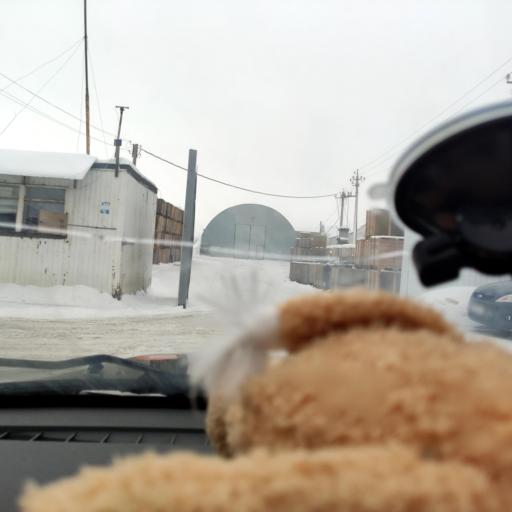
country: RU
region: Samara
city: Tol'yatti
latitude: 53.5774
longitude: 49.3215
